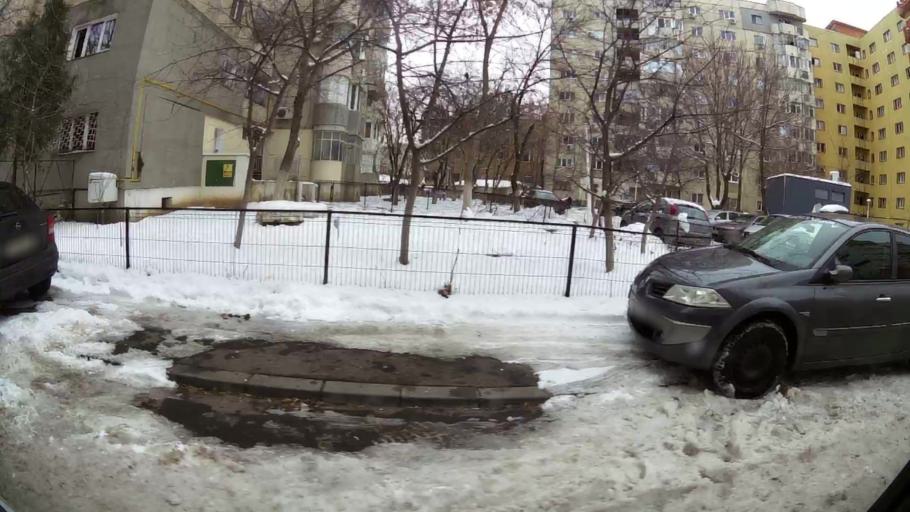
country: RO
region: Bucuresti
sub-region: Municipiul Bucuresti
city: Bucuresti
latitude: 44.3988
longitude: 26.1040
